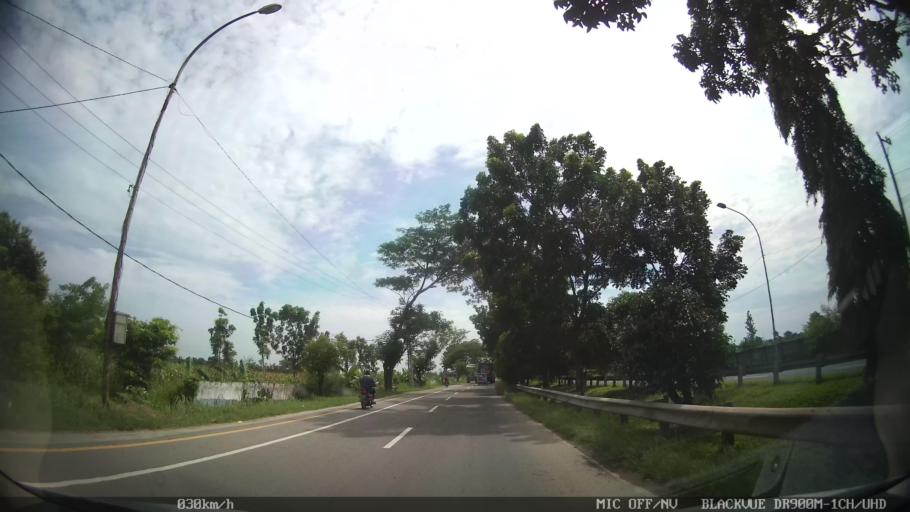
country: ID
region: North Sumatra
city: Percut
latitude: 3.5963
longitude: 98.8084
